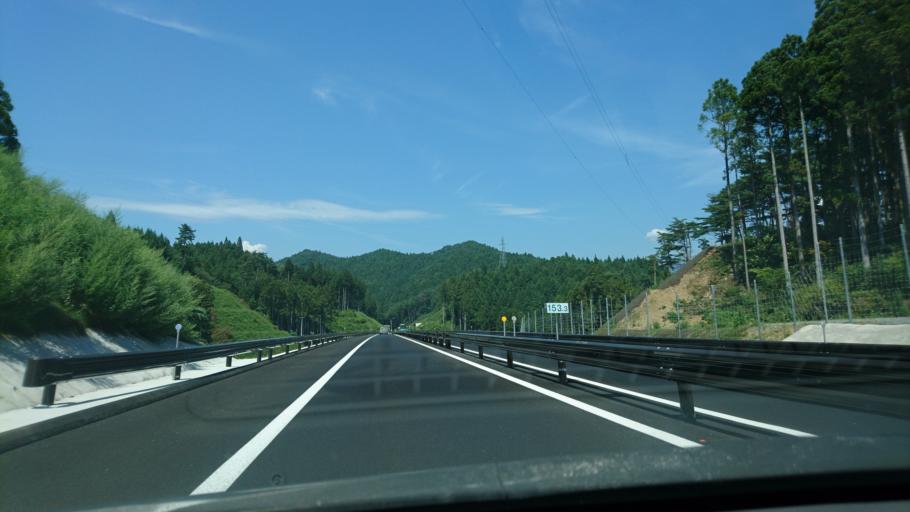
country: JP
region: Iwate
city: Ofunato
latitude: 39.0130
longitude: 141.6091
